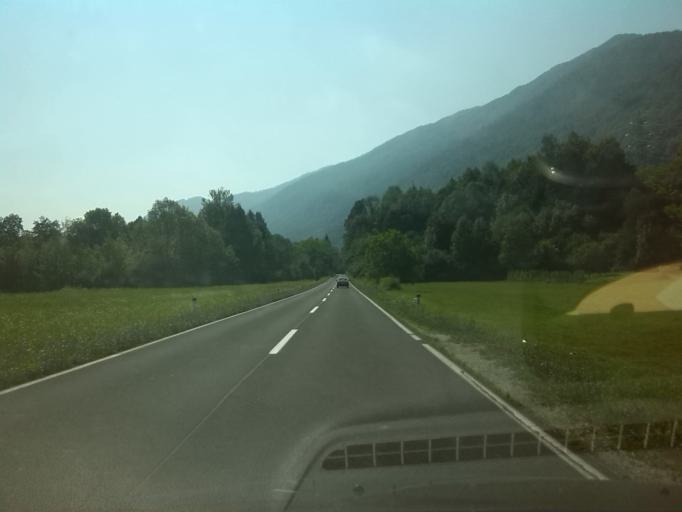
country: SI
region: Kobarid
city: Kobarid
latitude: 46.2233
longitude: 13.6031
